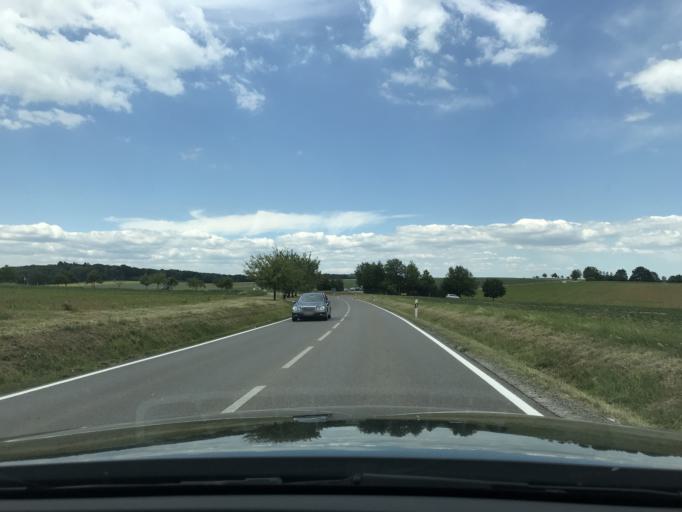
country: DE
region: Baden-Wuerttemberg
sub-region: Regierungsbezirk Stuttgart
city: Schwaikheim
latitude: 48.8917
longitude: 9.3658
